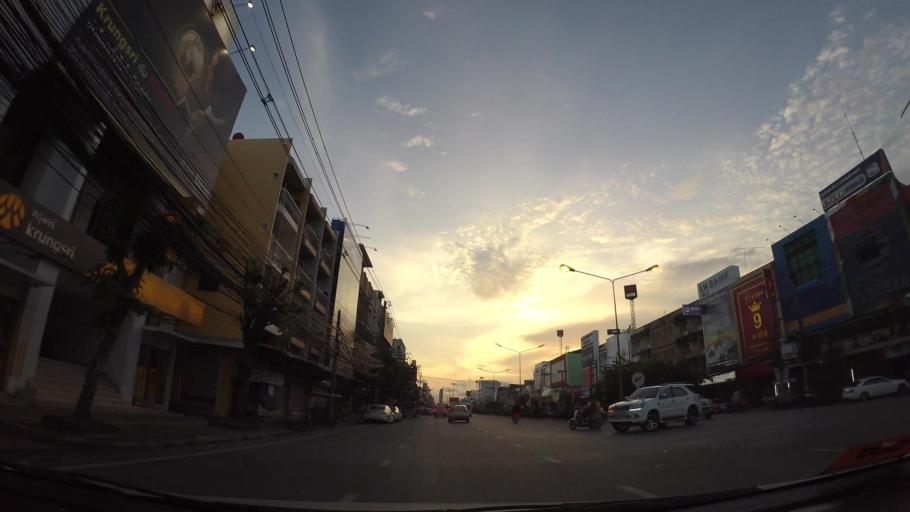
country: TH
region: Rayong
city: Rayong
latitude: 12.6818
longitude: 101.2731
